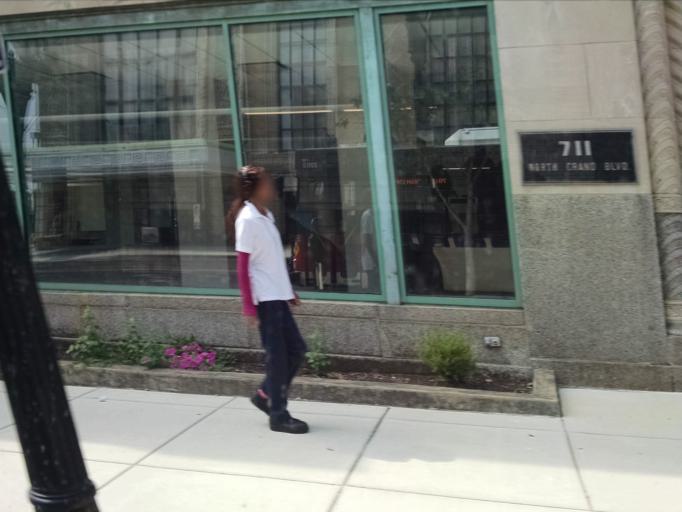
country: US
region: Missouri
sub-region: City of Saint Louis
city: St. Louis
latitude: 38.6405
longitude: -90.2307
